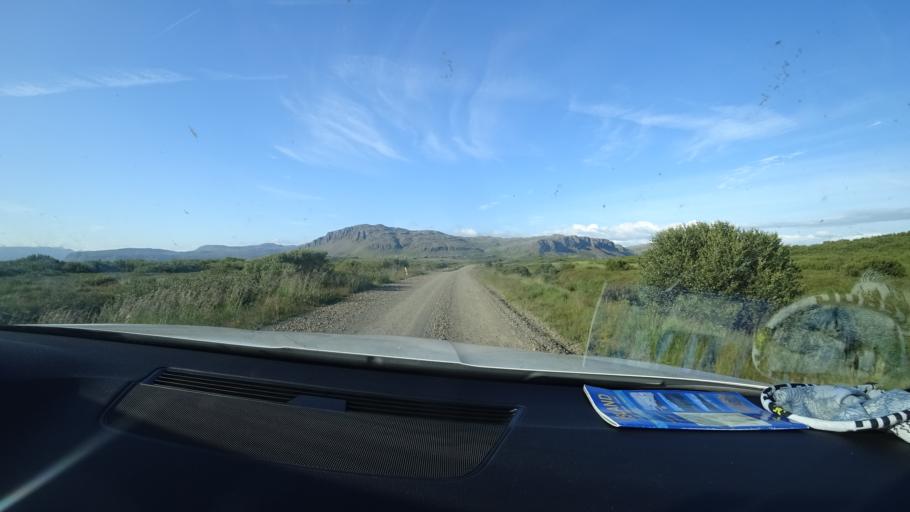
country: IS
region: West
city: Borgarnes
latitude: 64.6789
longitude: -21.9547
